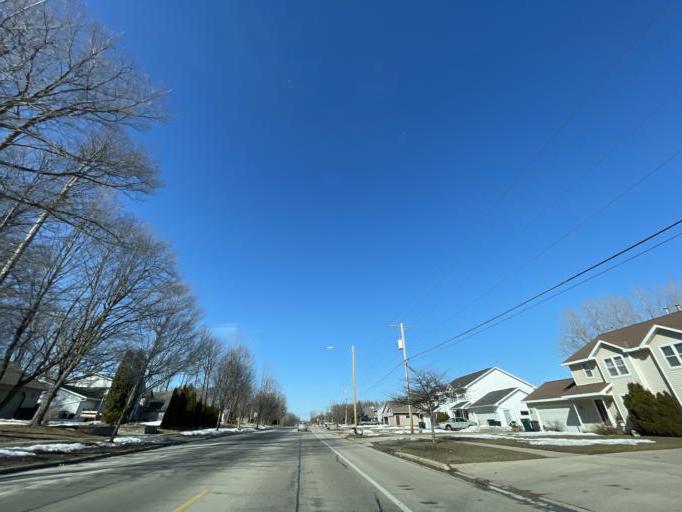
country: US
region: Wisconsin
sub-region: Brown County
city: Howard
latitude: 44.5827
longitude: -88.0845
